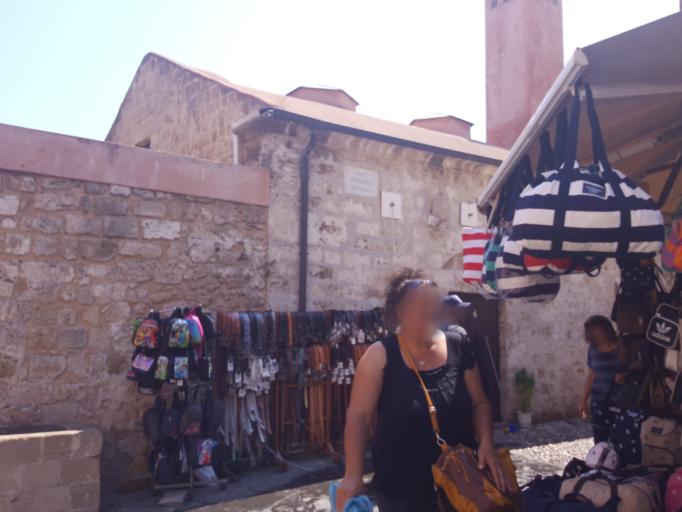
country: GR
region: South Aegean
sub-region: Nomos Dodekanisou
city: Rodos
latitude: 36.4439
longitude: 28.2242
